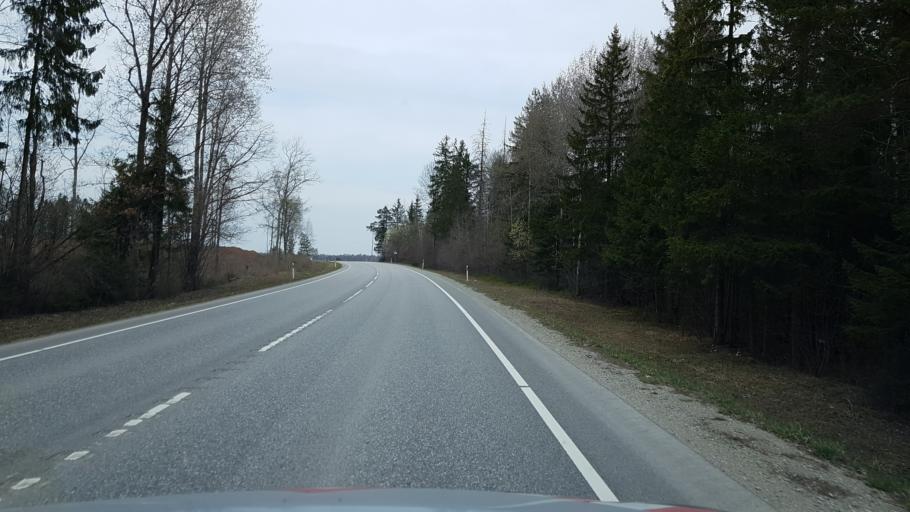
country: EE
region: Laeaene-Virumaa
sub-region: Someru vald
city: Someru
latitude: 59.3418
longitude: 26.4115
